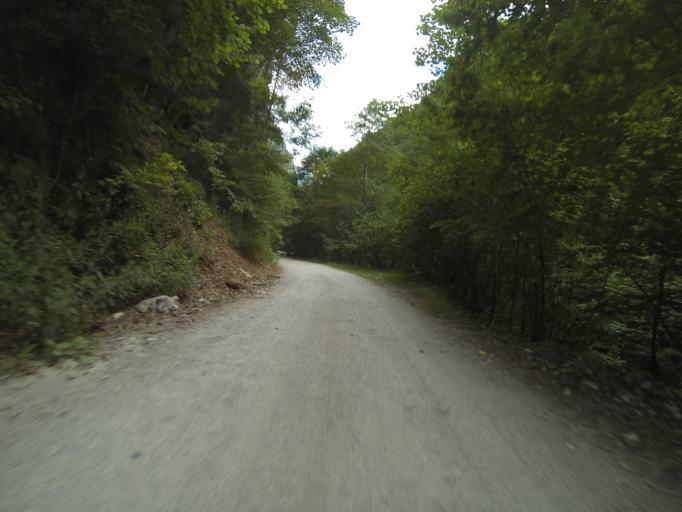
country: RO
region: Gorj
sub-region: Comuna Polovragi
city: Polovragi
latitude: 45.2098
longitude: 23.7767
